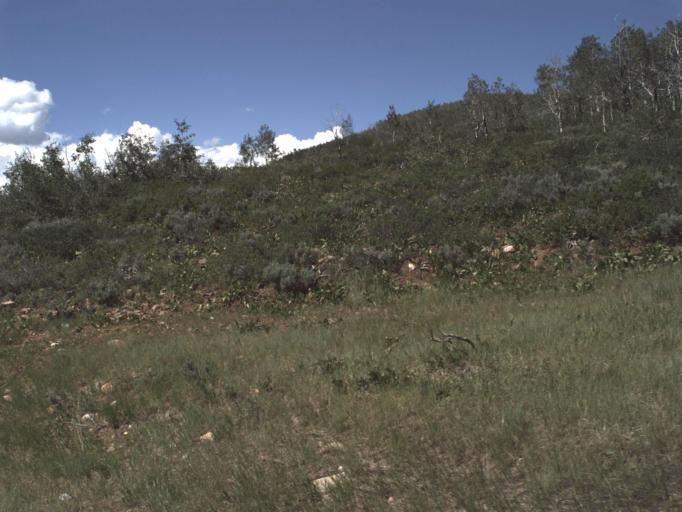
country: US
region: Utah
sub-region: Weber County
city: Wolf Creek
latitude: 41.4063
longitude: -111.5506
